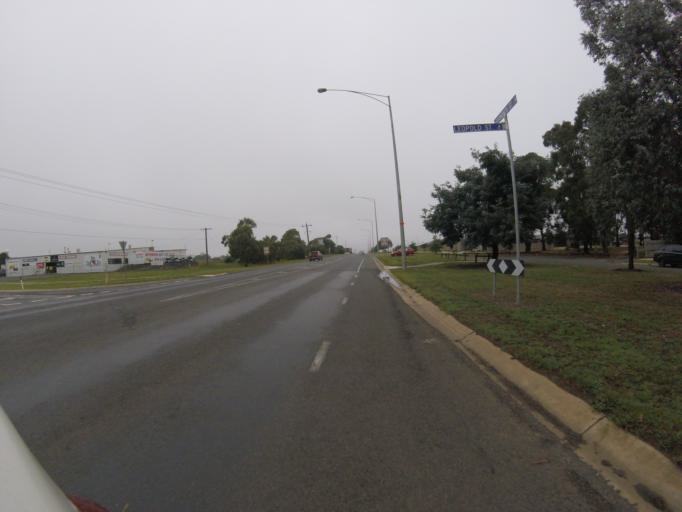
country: AU
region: Victoria
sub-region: Ballarat North
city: Newington
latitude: -37.5583
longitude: 143.8125
